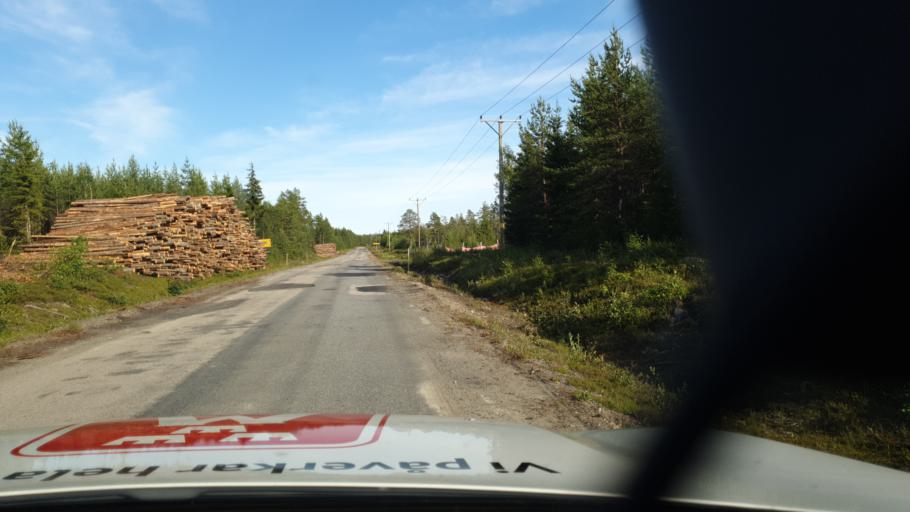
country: SE
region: Vaesterbotten
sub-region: Umea Kommun
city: Saevar
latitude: 63.8704
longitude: 20.7206
